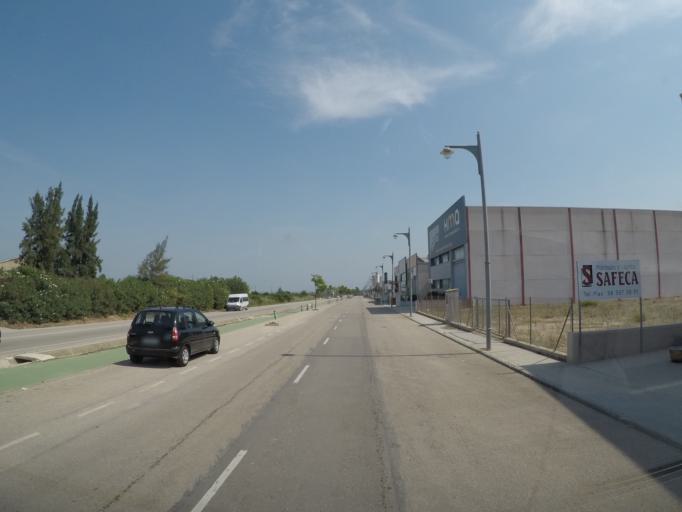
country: ES
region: Valencia
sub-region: Provincia de Alicante
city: Pego
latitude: 38.8446
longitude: -0.1020
